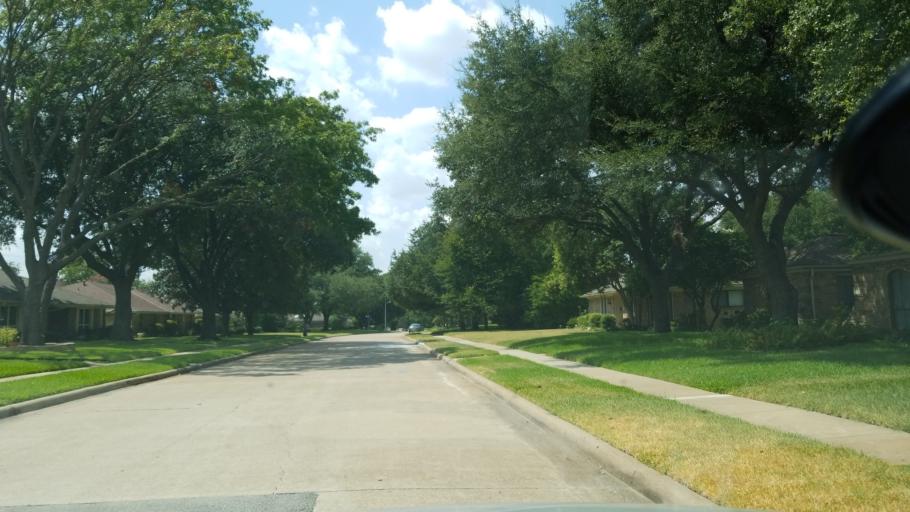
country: US
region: Texas
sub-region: Dallas County
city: Richardson
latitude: 32.9259
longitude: -96.7226
